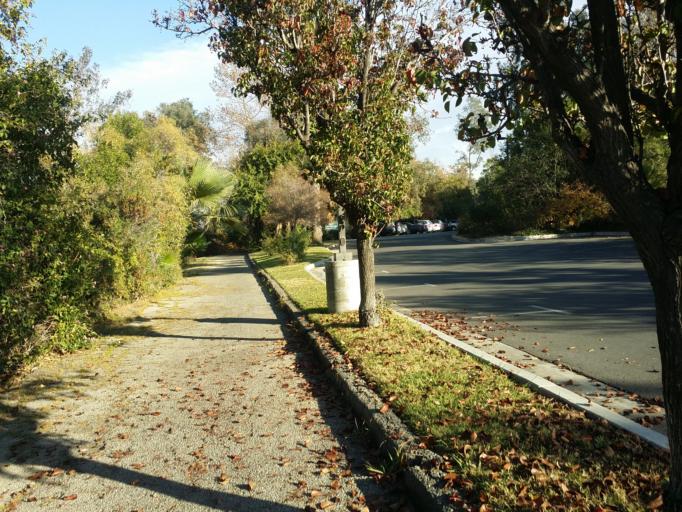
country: US
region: California
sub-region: San Bernardino County
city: Redlands
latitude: 34.0587
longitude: -117.1943
